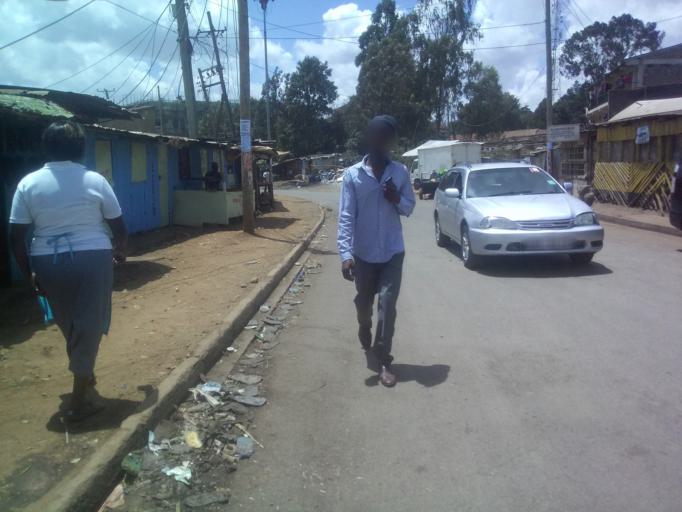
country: KE
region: Nairobi Area
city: Nairobi
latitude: -1.3093
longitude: 36.7783
